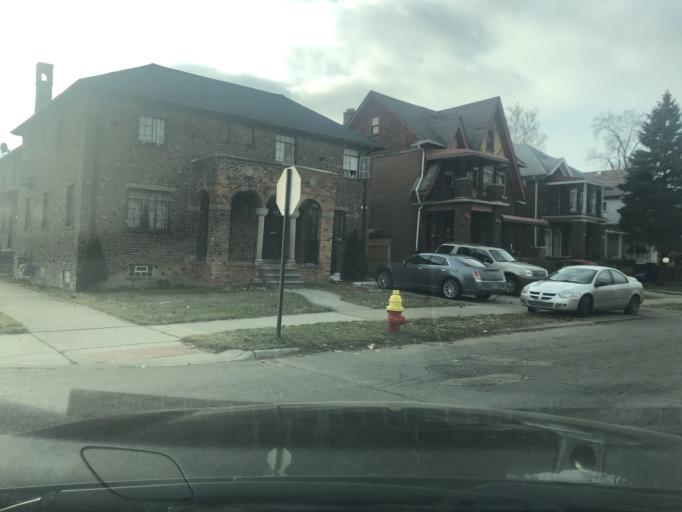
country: US
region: Michigan
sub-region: Wayne County
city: Highland Park
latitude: 42.3867
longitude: -83.1347
